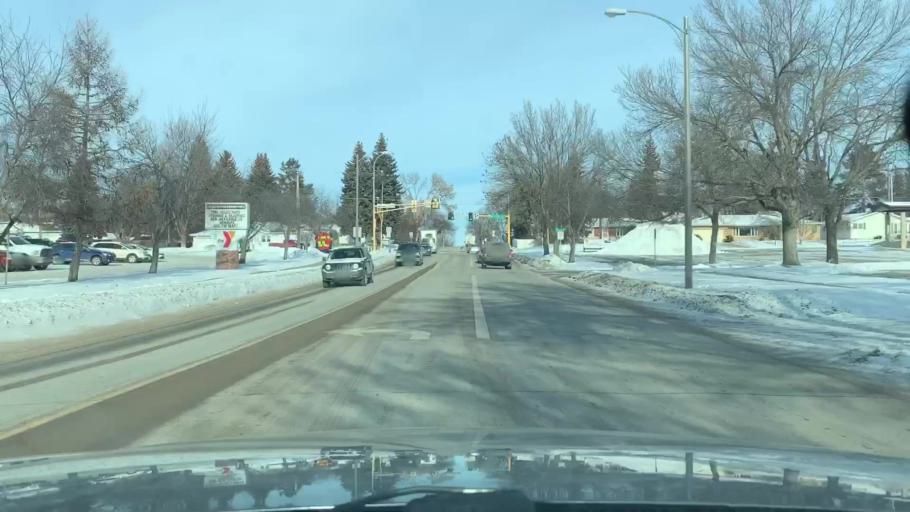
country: US
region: North Dakota
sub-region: Burleigh County
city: Bismarck
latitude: 46.8227
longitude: -100.7941
